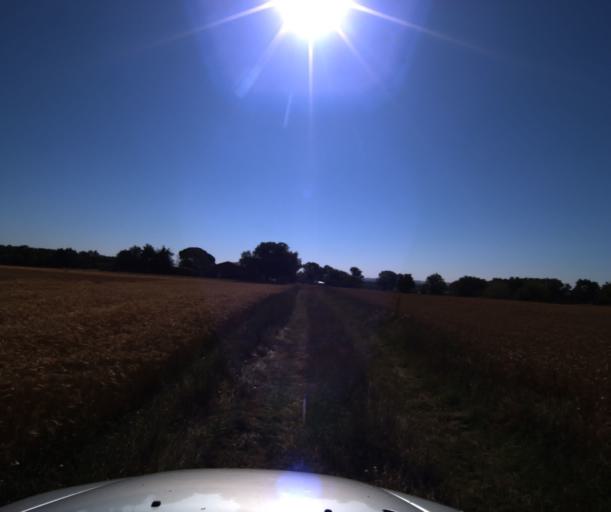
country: FR
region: Midi-Pyrenees
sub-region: Departement de la Haute-Garonne
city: Eaunes
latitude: 43.4202
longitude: 1.3604
